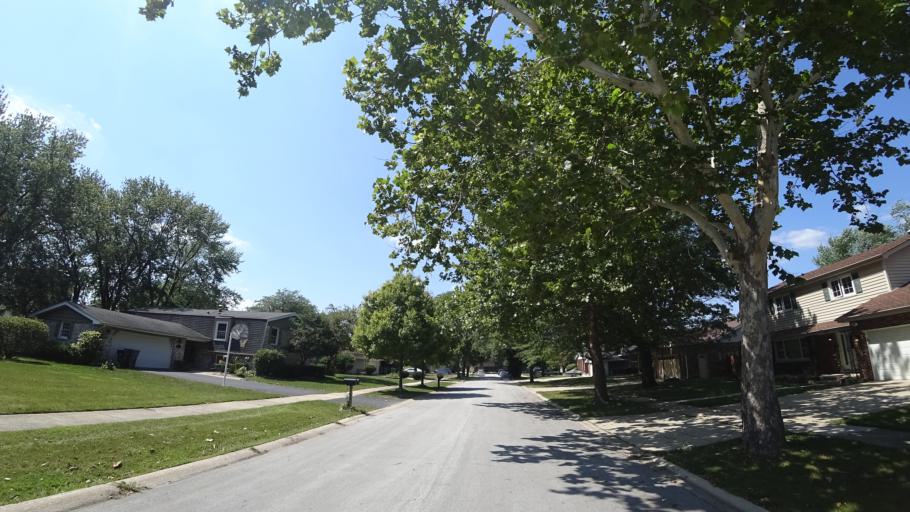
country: US
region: Illinois
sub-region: Cook County
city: Orland Park
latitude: 41.6269
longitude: -87.8300
